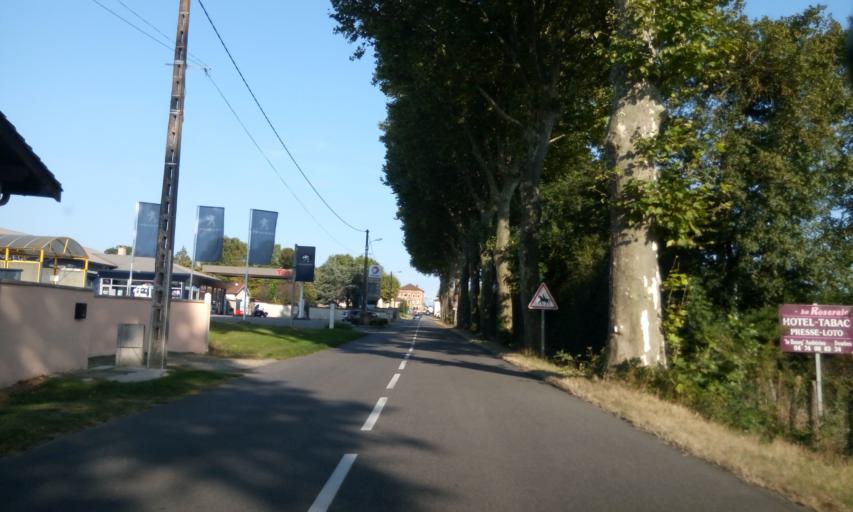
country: FR
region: Rhone-Alpes
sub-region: Departement de l'Ain
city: Amberieux-en-Dombes
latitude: 45.9988
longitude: 4.8979
